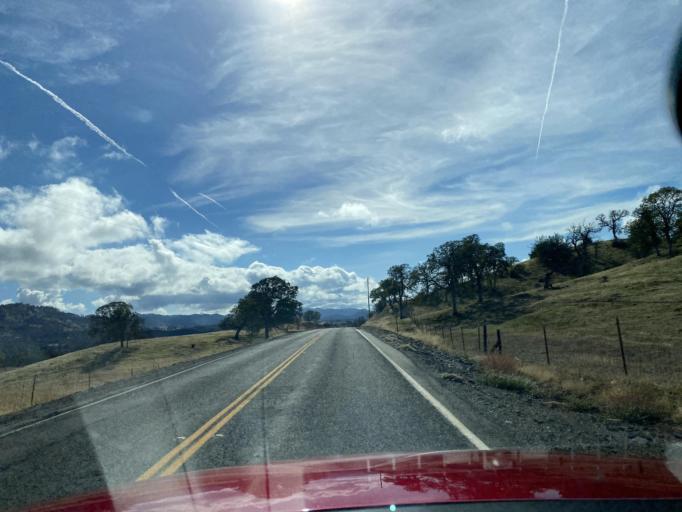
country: US
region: California
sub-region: Glenn County
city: Willows
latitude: 39.4750
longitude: -122.5139
